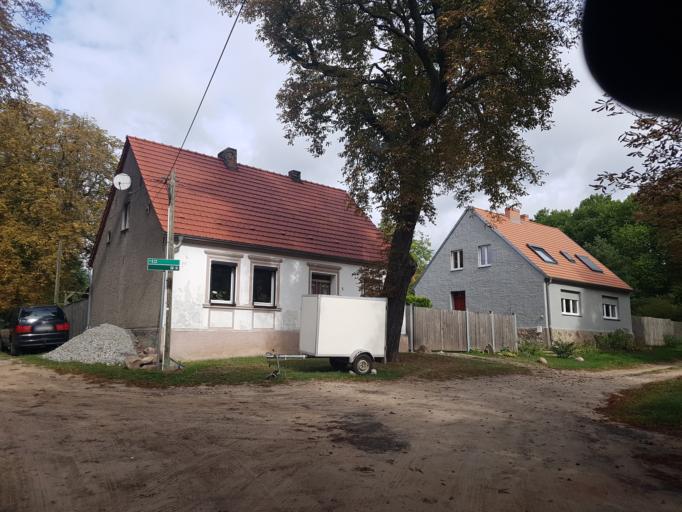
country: DE
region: Brandenburg
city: Gorzke
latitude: 52.1182
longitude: 12.3770
